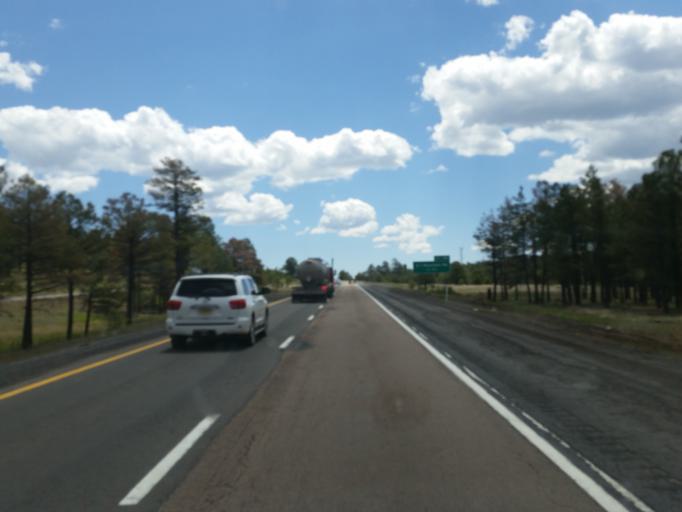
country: US
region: Arizona
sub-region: Coconino County
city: Flagstaff
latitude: 35.2007
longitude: -111.7584
